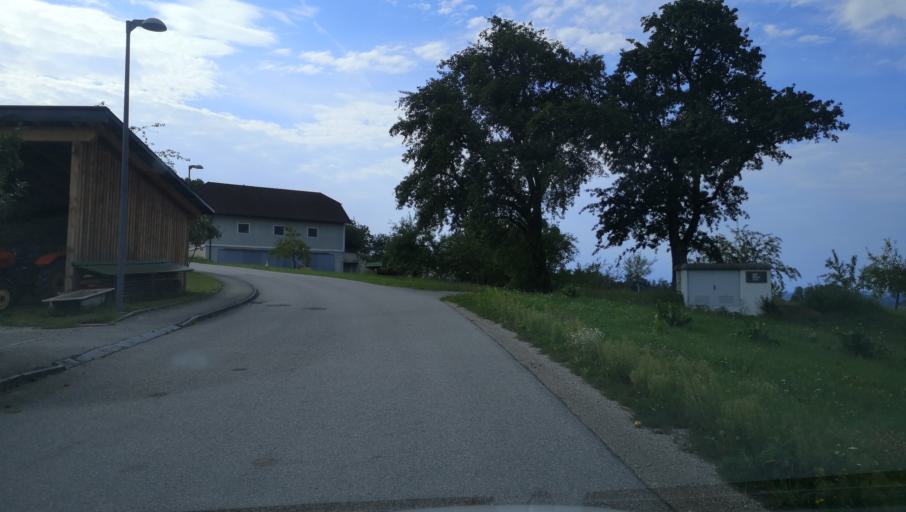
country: AT
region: Lower Austria
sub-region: Politischer Bezirk Amstetten
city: Zeillern
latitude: 48.1583
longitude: 14.8208
